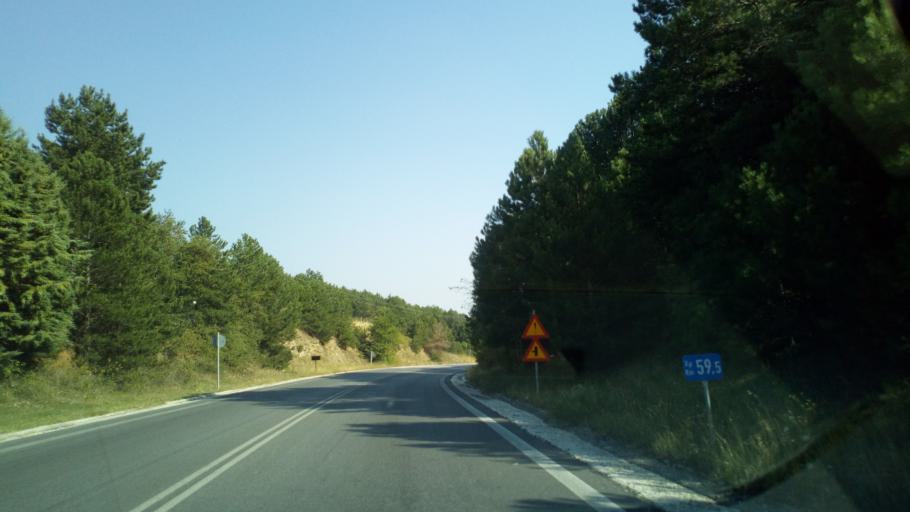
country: GR
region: Central Macedonia
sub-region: Nomos Chalkidikis
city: Polygyros
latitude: 40.4005
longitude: 23.4247
